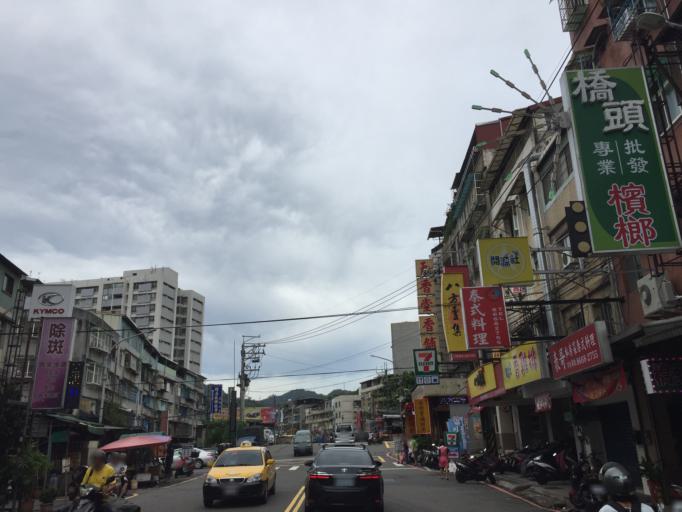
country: TW
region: Taipei
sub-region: Taipei
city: Banqiao
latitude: 24.9847
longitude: 121.5059
